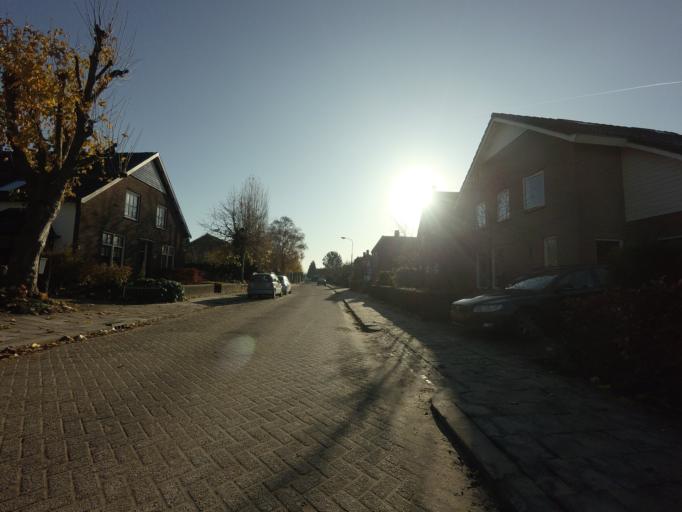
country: NL
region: Gelderland
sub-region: Gemeente Maasdriel
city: Heerewaarden
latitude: 51.7682
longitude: 5.3417
